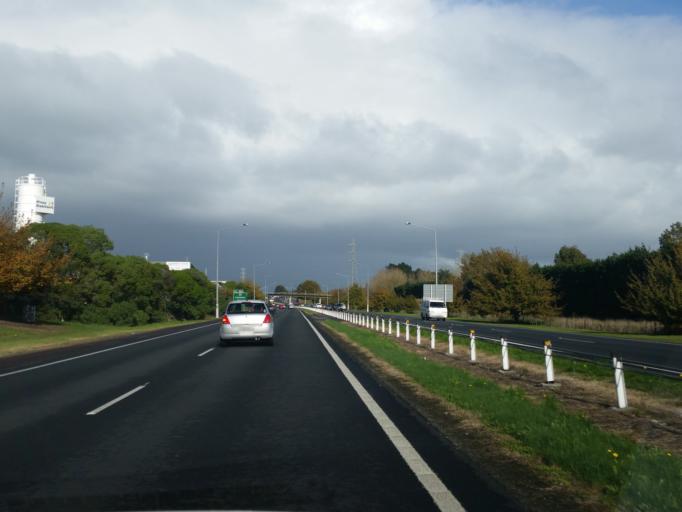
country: NZ
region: Auckland
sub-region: Auckland
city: Papakura
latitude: -37.1000
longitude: 174.9450
